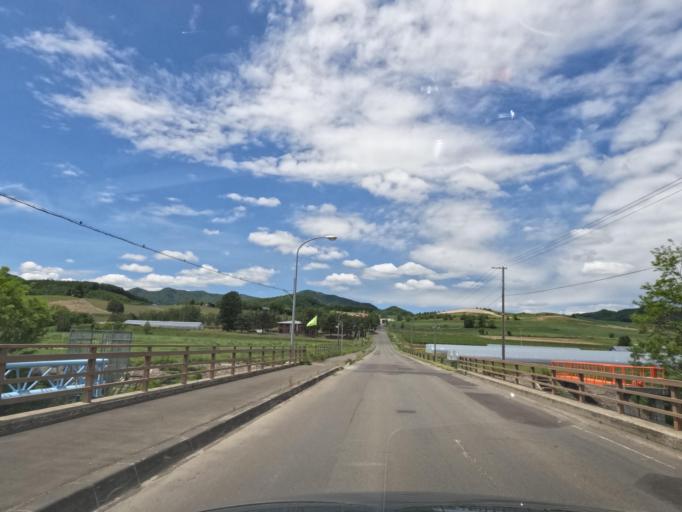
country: JP
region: Hokkaido
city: Shimo-furano
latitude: 43.3677
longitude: 142.3825
